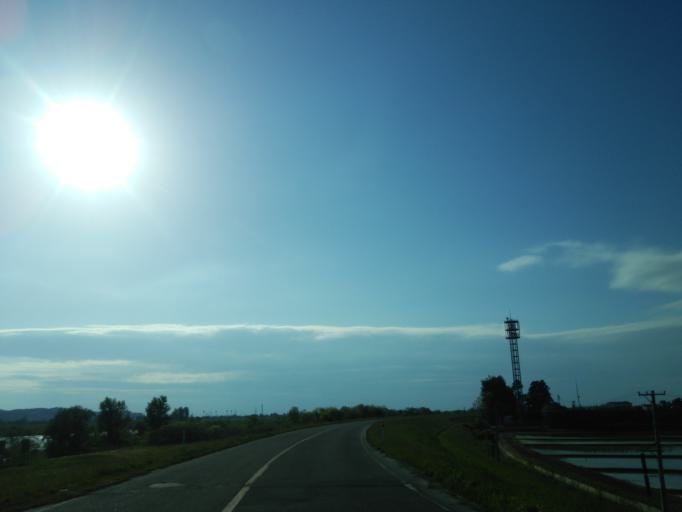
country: JP
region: Niigata
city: Gosen
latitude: 37.7833
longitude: 139.1887
